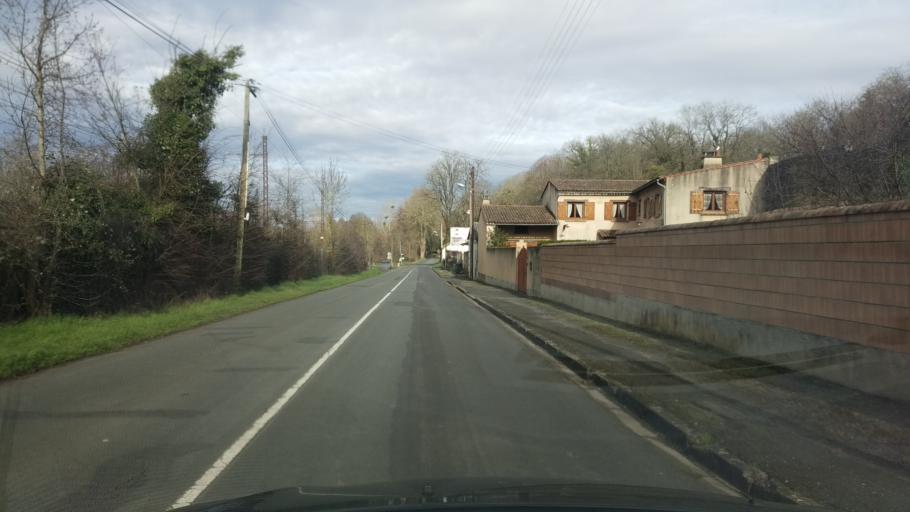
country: FR
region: Poitou-Charentes
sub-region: Departement de la Vienne
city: Poitiers
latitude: 46.6020
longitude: 0.3453
